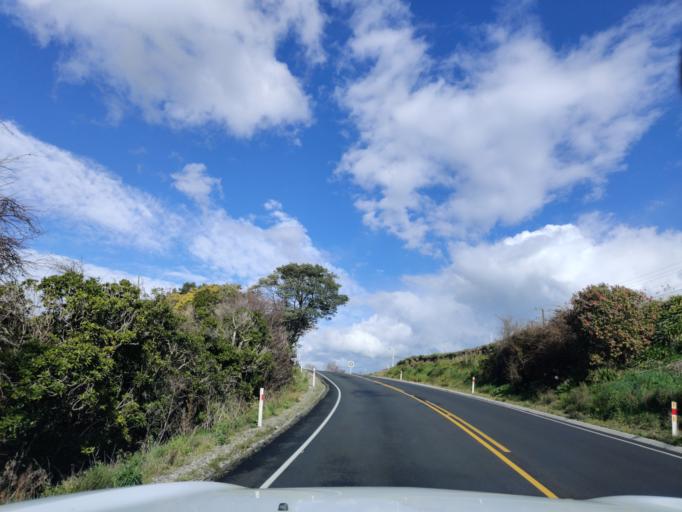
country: NZ
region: Manawatu-Wanganui
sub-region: Palmerston North City
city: Palmerston North
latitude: -40.2806
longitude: 175.7605
